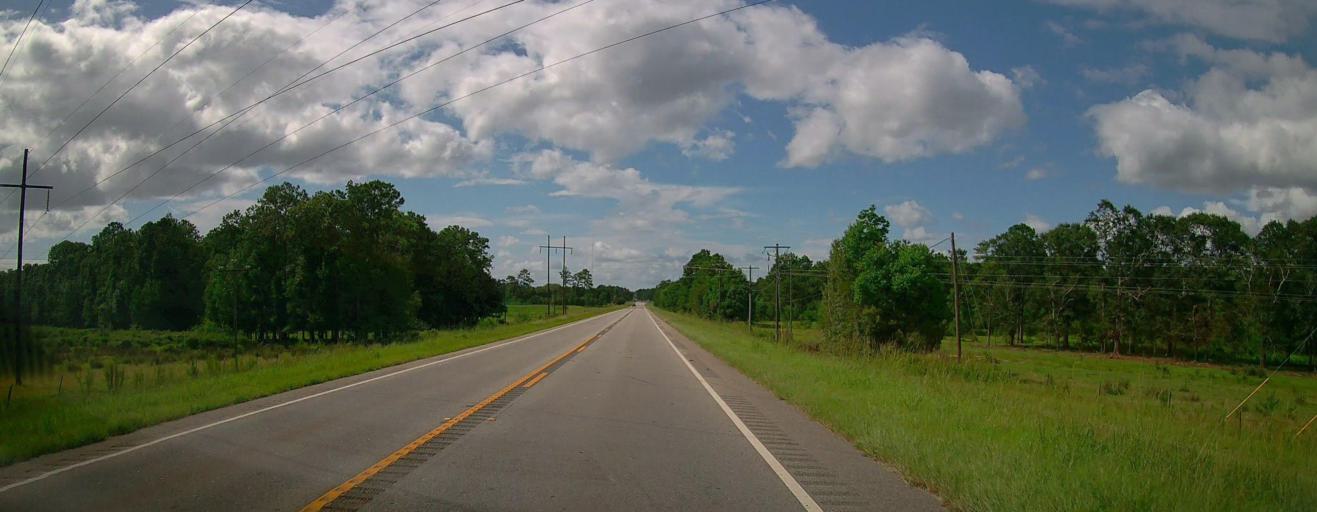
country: US
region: Georgia
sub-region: Coffee County
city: Douglas
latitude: 31.5324
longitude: -82.8808
